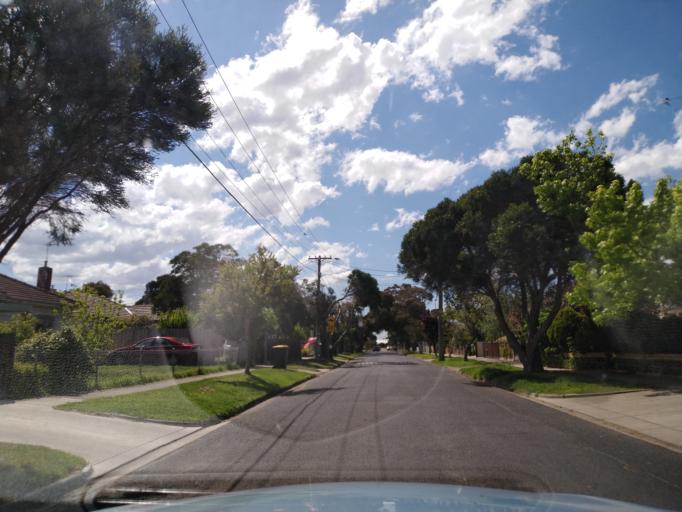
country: AU
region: Victoria
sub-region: Hobsons Bay
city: South Kingsville
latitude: -37.8296
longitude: 144.8688
